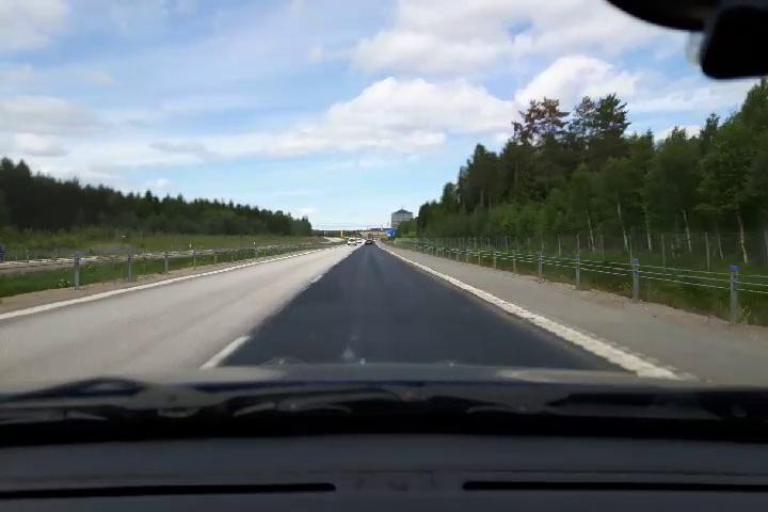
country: SE
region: Uppsala
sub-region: Alvkarleby Kommun
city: AElvkarleby
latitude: 60.4544
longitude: 17.4154
